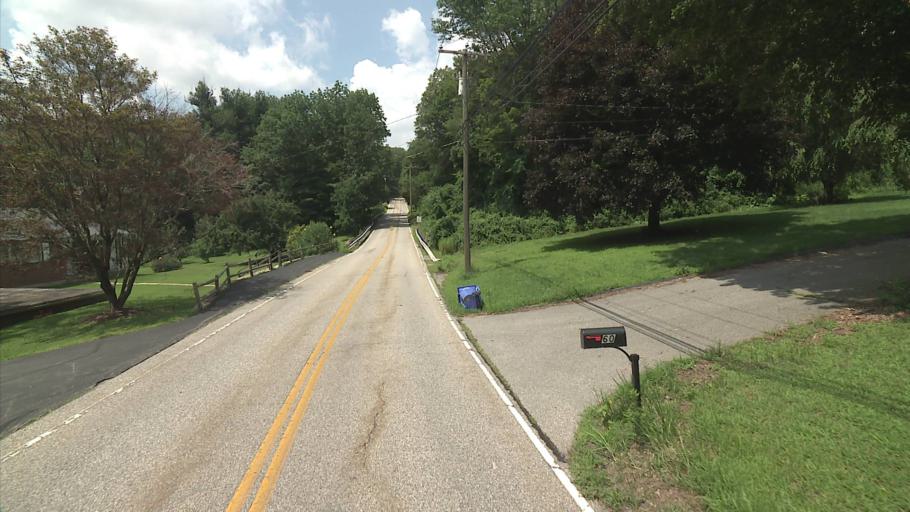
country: US
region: Connecticut
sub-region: New London County
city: Baltic
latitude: 41.6128
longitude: -72.0626
